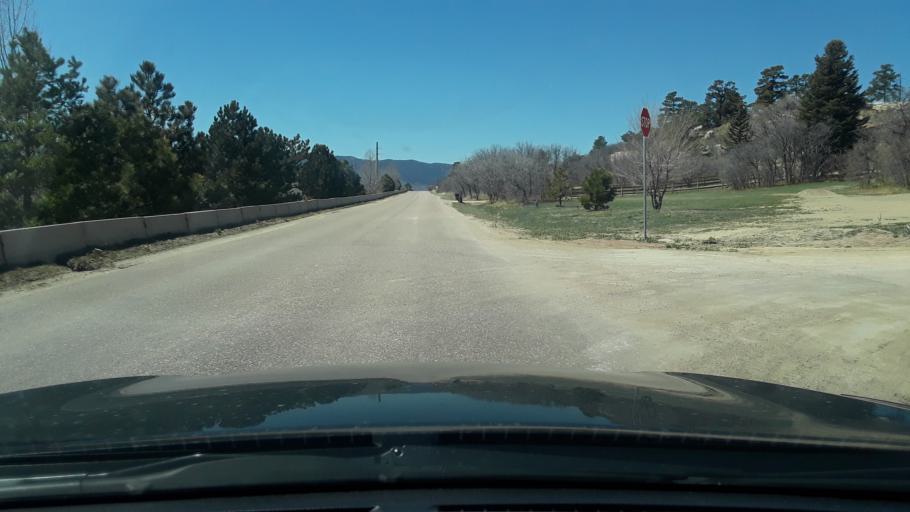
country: US
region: Colorado
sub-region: El Paso County
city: Gleneagle
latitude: 39.0347
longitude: -104.7800
